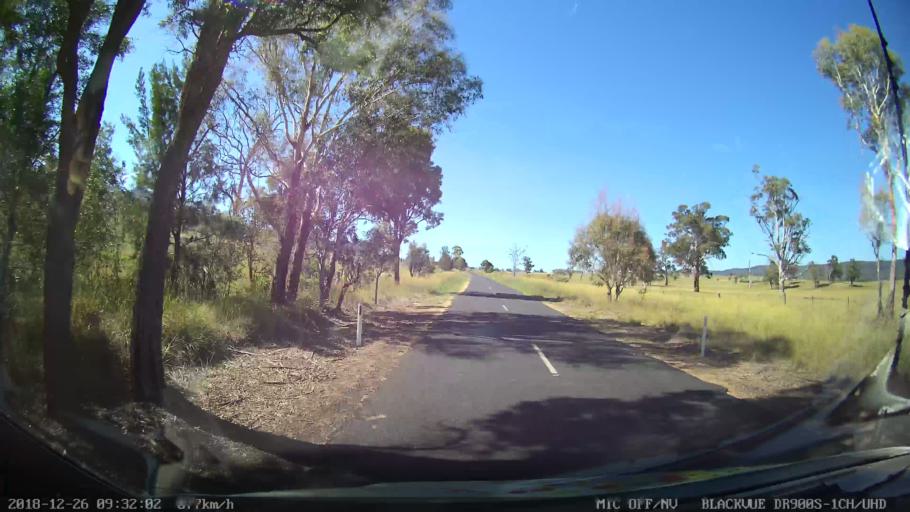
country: AU
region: New South Wales
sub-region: Mid-Western Regional
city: Kandos
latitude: -32.8796
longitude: 150.0321
